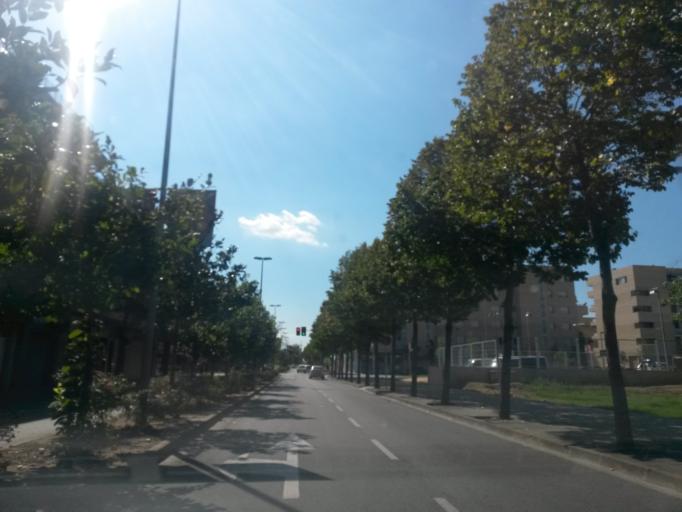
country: ES
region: Catalonia
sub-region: Provincia de Girona
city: Salt
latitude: 41.9693
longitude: 2.7870
